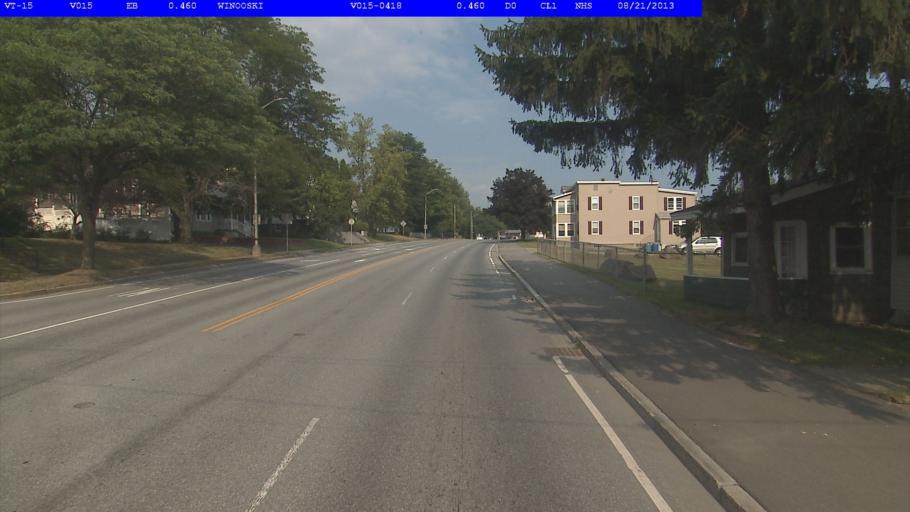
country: US
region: Vermont
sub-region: Chittenden County
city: Winooski
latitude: 44.4928
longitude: -73.1775
